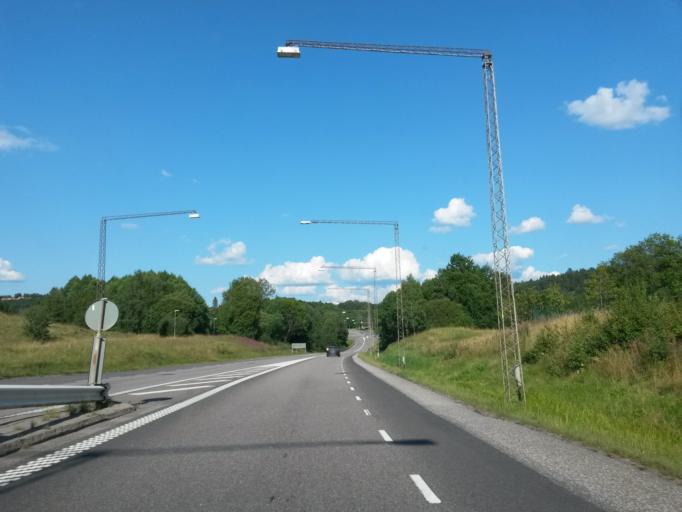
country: SE
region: Vaestra Goetaland
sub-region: Goteborg
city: Eriksbo
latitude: 57.7769
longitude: 12.0655
